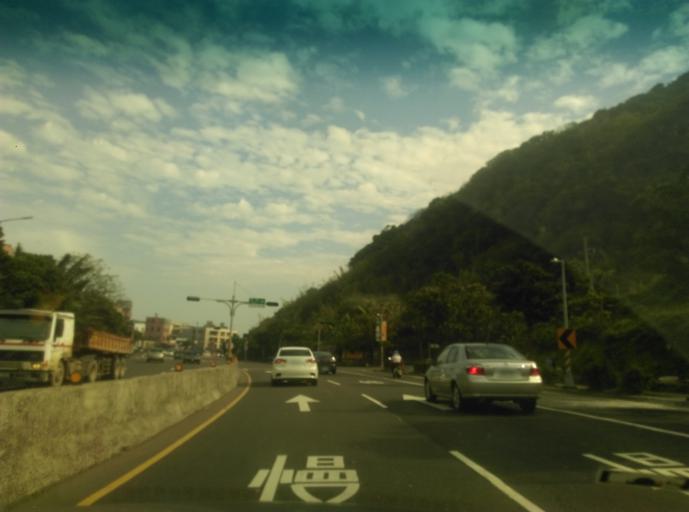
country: TW
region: Taiwan
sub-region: Keelung
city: Keelung
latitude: 25.1854
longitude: 121.6840
